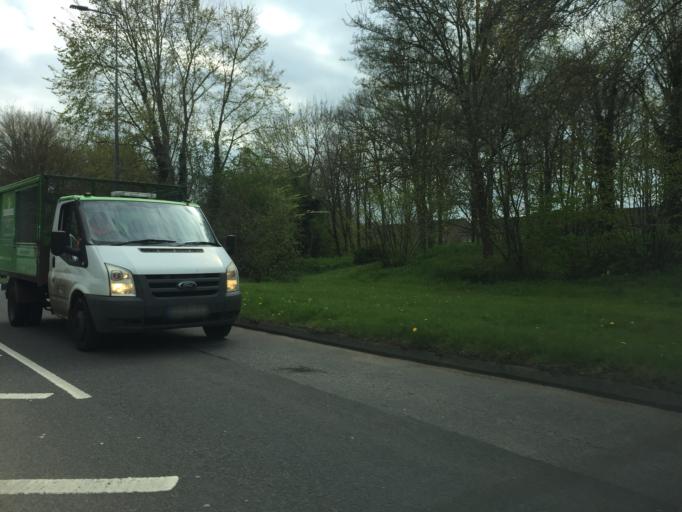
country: GB
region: England
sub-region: Milton Keynes
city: Milton Keynes
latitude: 52.0632
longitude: -0.7588
